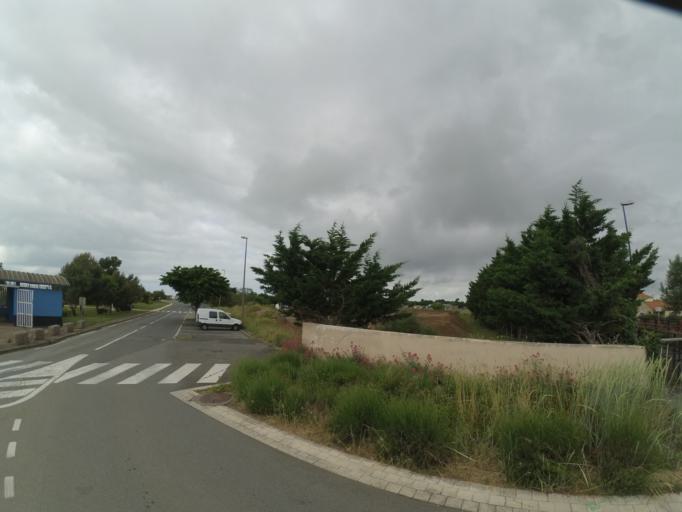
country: FR
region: Poitou-Charentes
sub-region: Departement de la Charente-Maritime
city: Aytre
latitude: 46.1276
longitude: -1.1285
